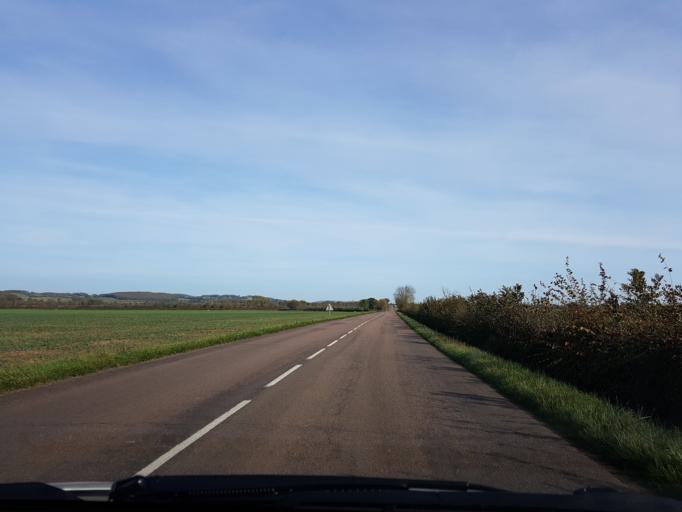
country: FR
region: Bourgogne
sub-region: Departement de la Cote-d'Or
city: Semur-en-Auxois
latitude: 47.4994
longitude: 4.1303
